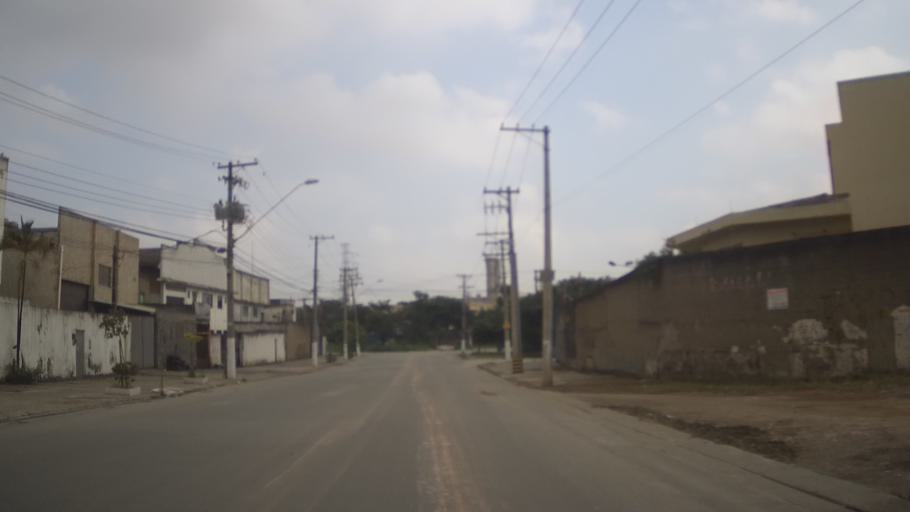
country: BR
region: Sao Paulo
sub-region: Guarulhos
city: Guarulhos
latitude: -23.4666
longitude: -46.4700
